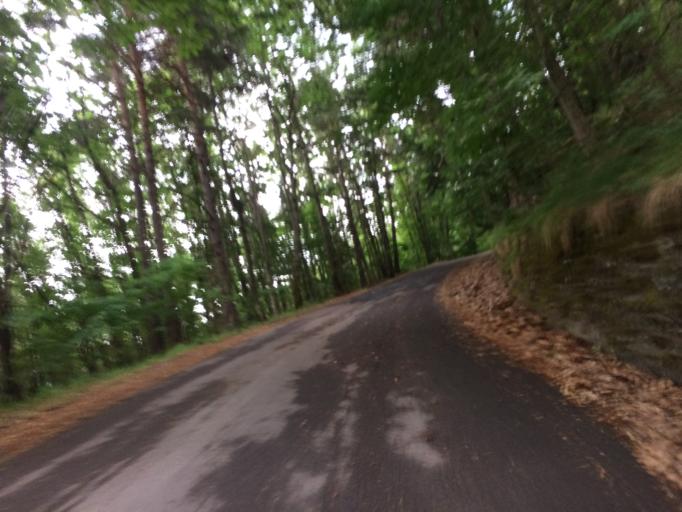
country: IT
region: Liguria
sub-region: Provincia di Imperia
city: Triora
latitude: 43.9817
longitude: 7.7530
